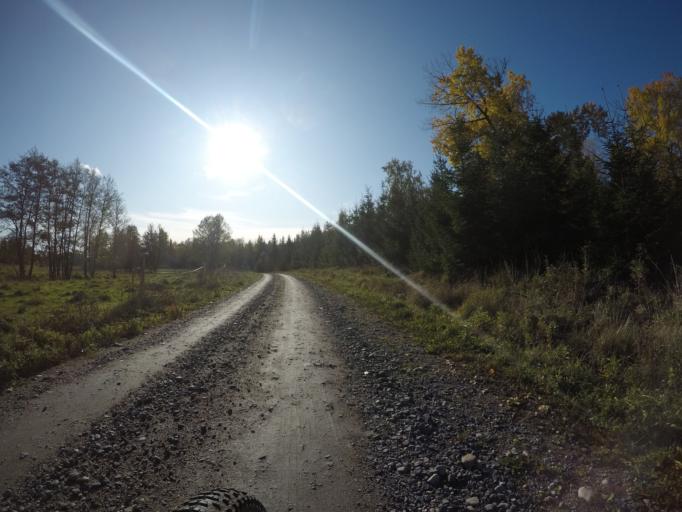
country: SE
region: Vaestmanland
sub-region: Kungsors Kommun
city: Kungsoer
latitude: 59.3202
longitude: 16.0886
